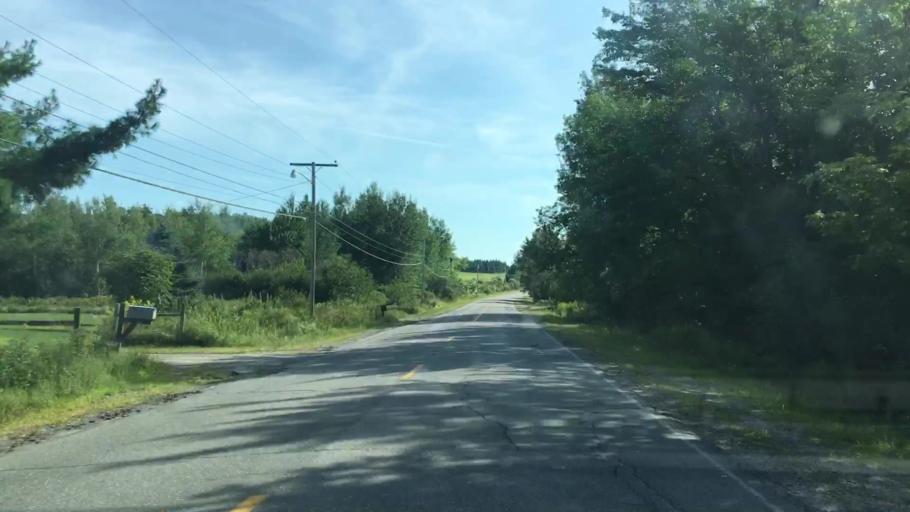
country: US
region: Maine
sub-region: Penobscot County
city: Lincoln
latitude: 45.3233
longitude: -68.5329
